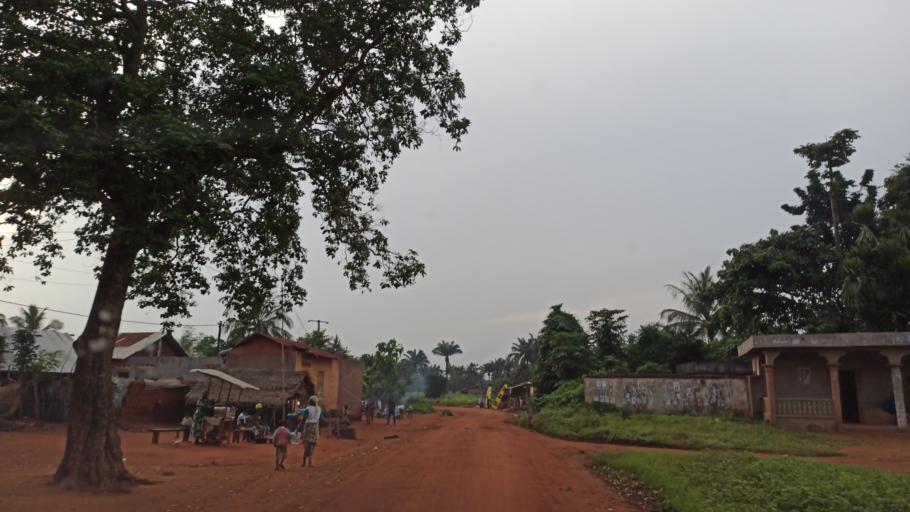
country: BJ
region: Queme
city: Porto-Novo
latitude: 6.5350
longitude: 2.6546
